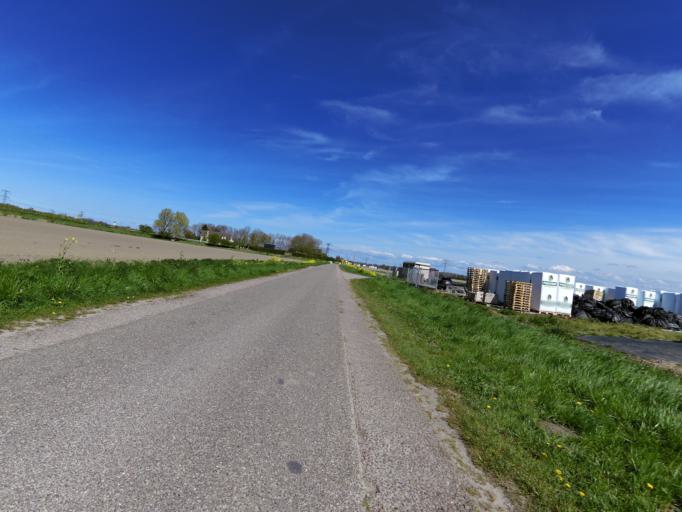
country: NL
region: South Holland
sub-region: Gemeente Brielle
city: Brielle
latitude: 51.8845
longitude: 4.1442
